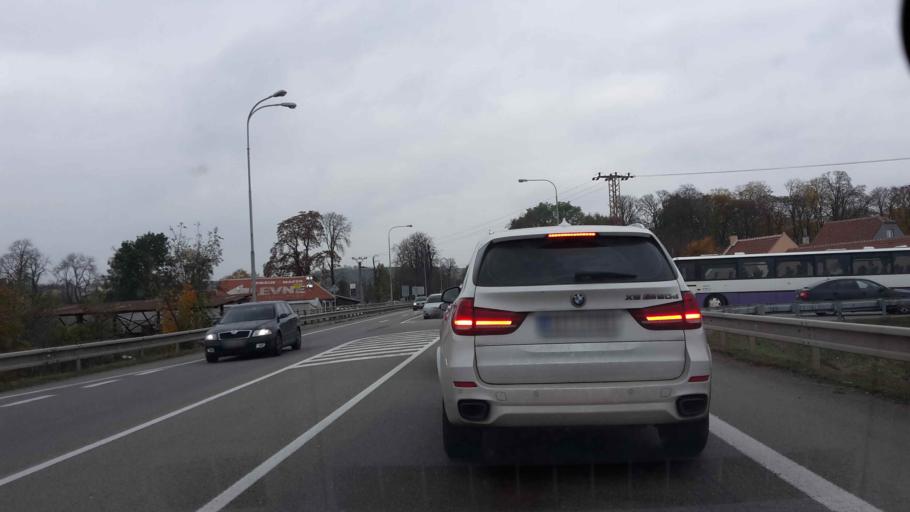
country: CZ
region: South Moravian
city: Slavkov u Brna
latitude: 49.1515
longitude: 16.8657
